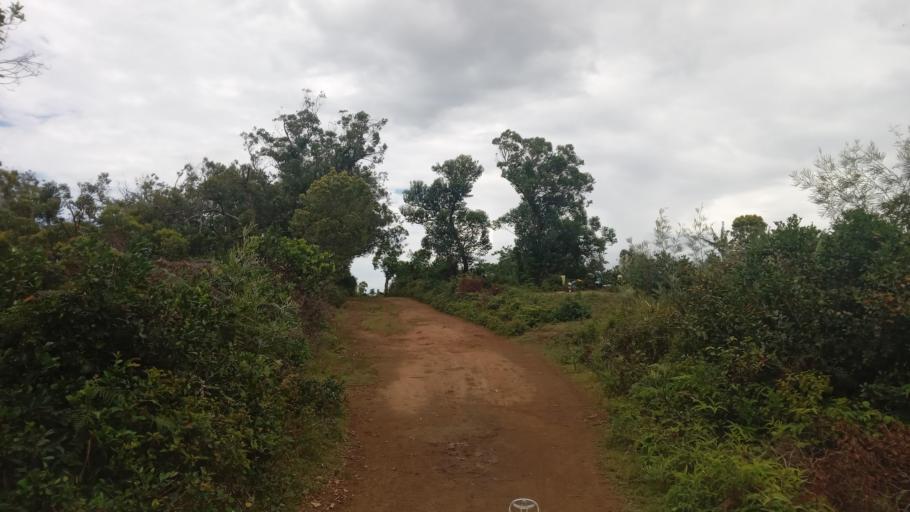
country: MG
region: Atsimo-Atsinanana
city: Vohipaho
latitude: -23.6195
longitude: 47.5799
